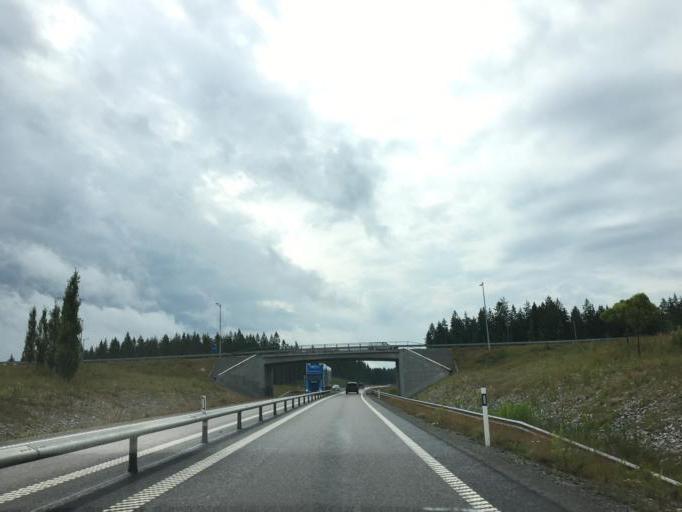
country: SE
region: Soedermanland
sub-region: Katrineholms Kommun
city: Katrineholm
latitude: 58.9946
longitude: 16.2588
